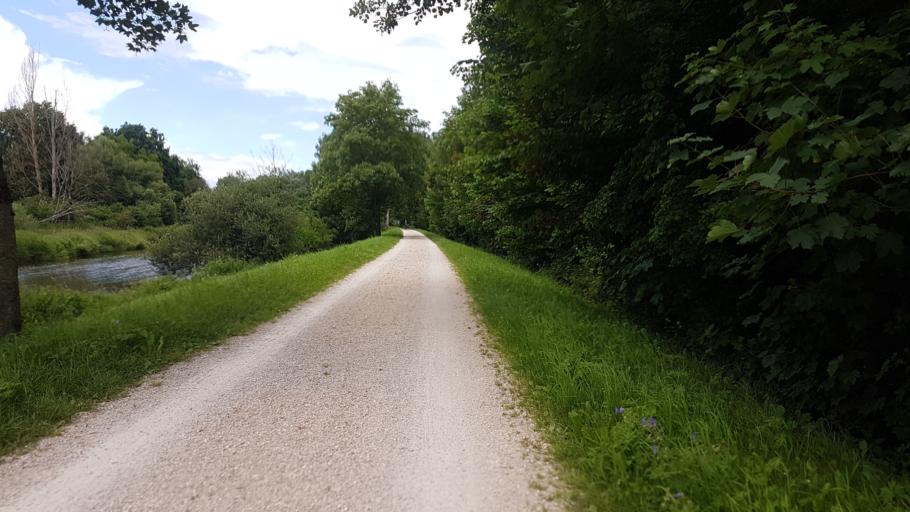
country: DE
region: Baden-Wuerttemberg
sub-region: Tuebingen Region
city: Neufra
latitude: 48.1414
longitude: 9.4736
